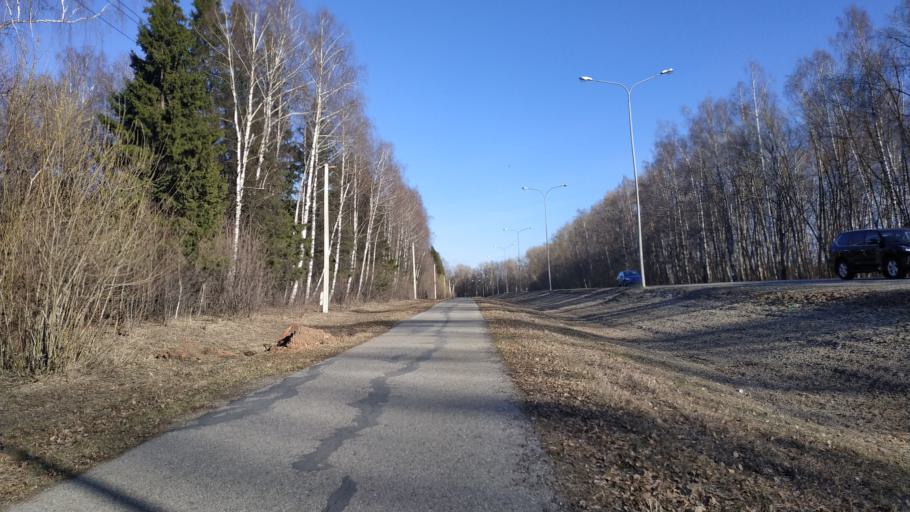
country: RU
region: Chuvashia
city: Novyye Lapsary
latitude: 56.1303
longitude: 47.1154
